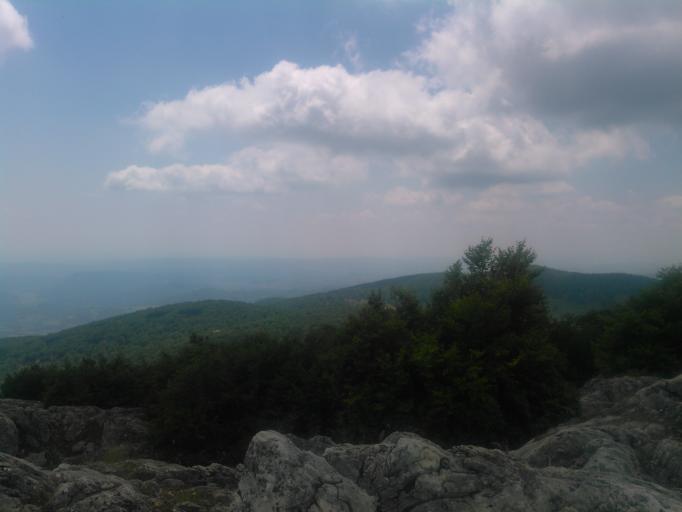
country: RO
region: Mehedinti
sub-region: Comuna Isverna
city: Isverna
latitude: 45.0248
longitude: 22.6015
